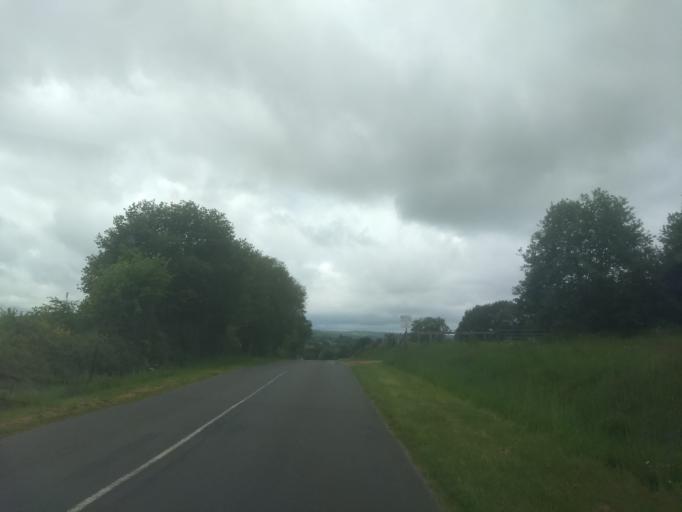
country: FR
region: Lower Normandy
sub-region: Departement de l'Orne
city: Bretoncelles
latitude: 48.4686
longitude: 0.8927
